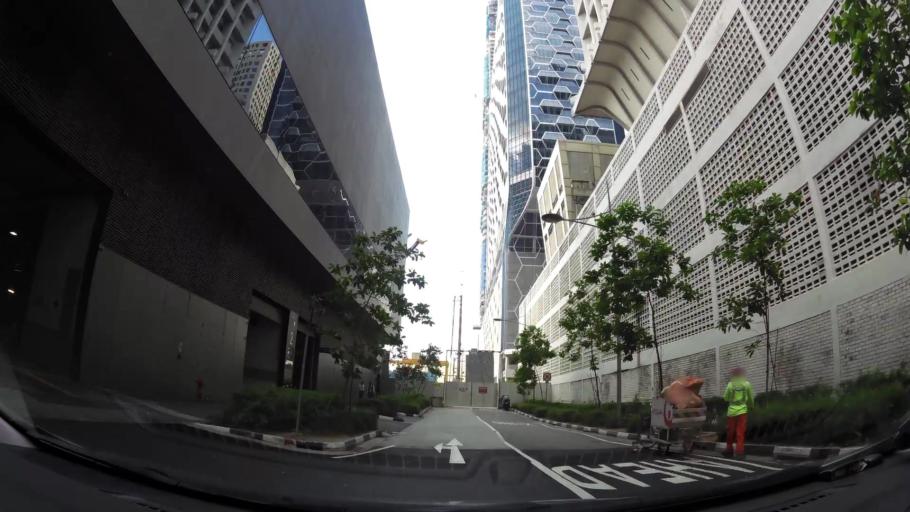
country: SG
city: Singapore
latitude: 1.2788
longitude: 103.8504
